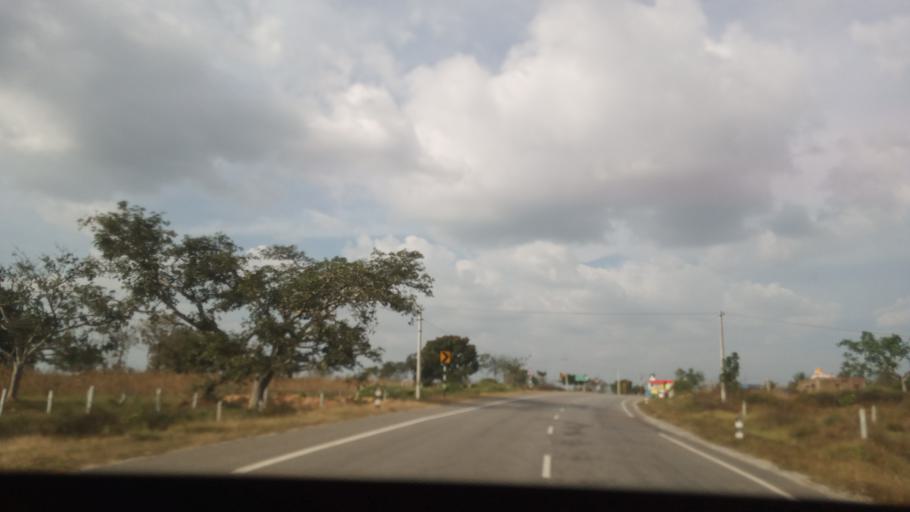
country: IN
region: Karnataka
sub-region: Tumkur
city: Kunigal
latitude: 12.8332
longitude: 77.0277
